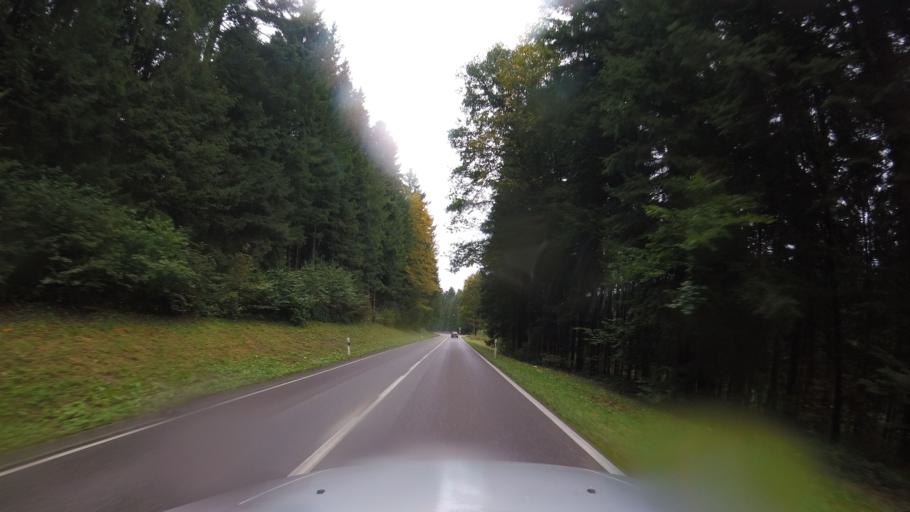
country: DE
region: Baden-Wuerttemberg
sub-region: Regierungsbezirk Stuttgart
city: Durlangen
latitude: 48.8460
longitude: 9.7800
